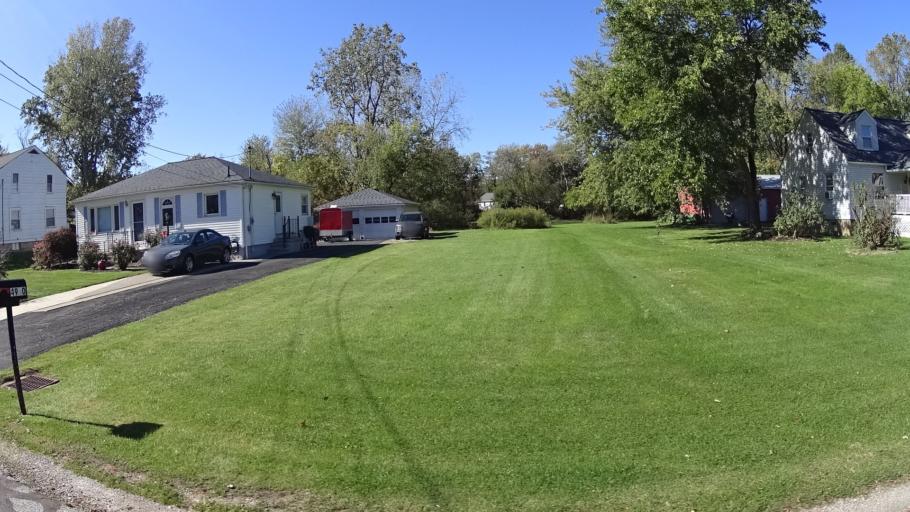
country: US
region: Ohio
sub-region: Lorain County
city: Lorain
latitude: 41.4236
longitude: -82.1589
